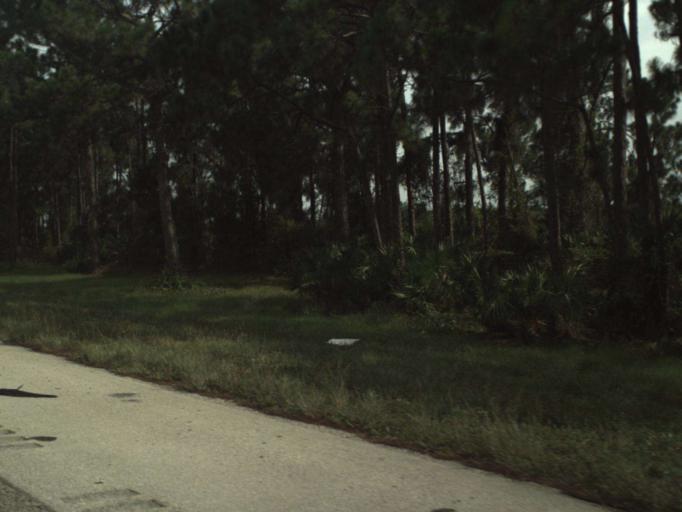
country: US
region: Florida
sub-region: Saint Lucie County
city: Port Saint Lucie
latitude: 27.2351
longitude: -80.4091
